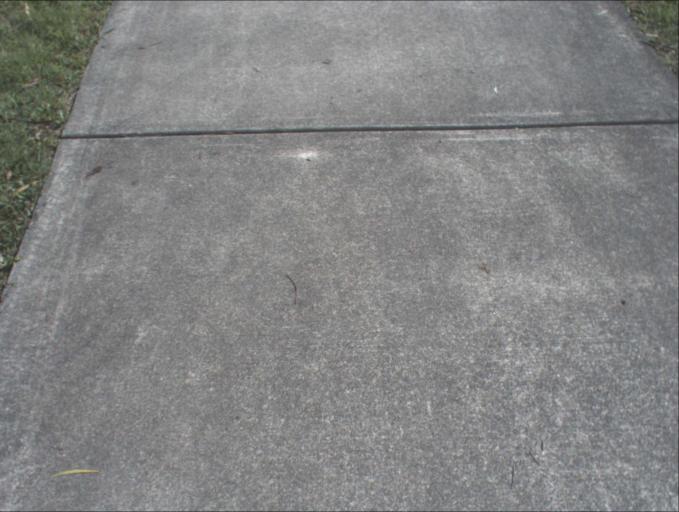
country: AU
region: Queensland
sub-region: Logan
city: Windaroo
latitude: -27.7220
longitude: 153.1737
